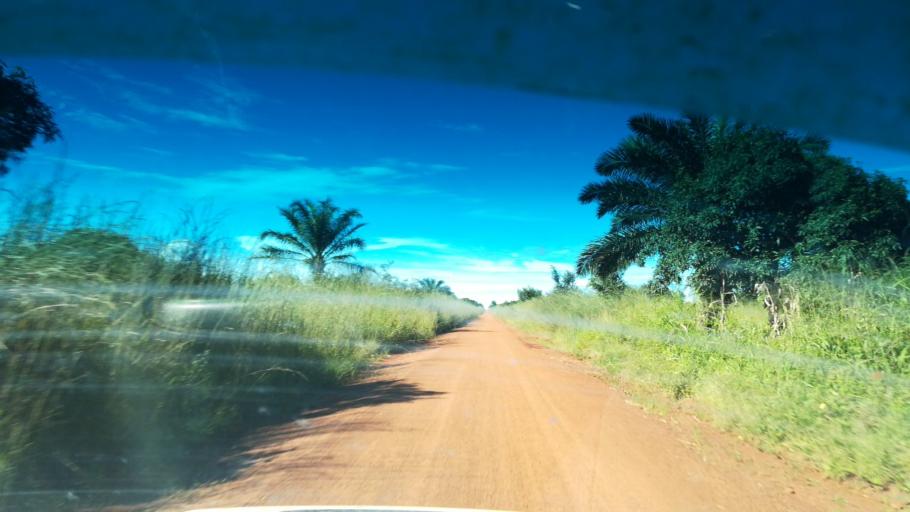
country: ZM
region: Luapula
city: Nchelenge
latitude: -9.3428
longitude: 28.2315
